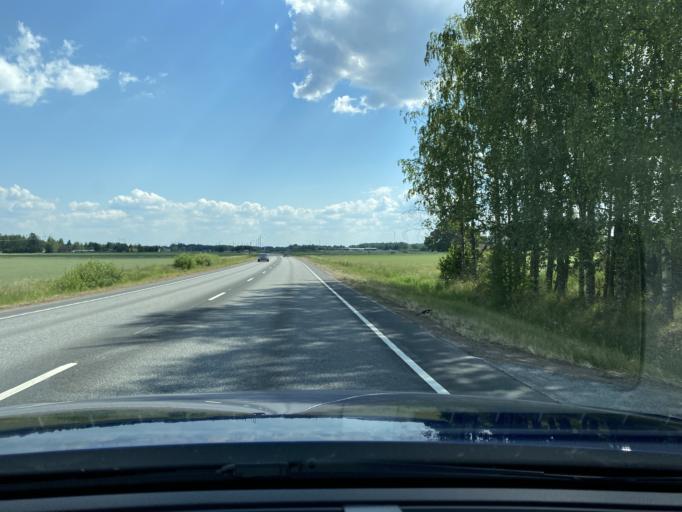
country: FI
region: Satakunta
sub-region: Rauma
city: Eura
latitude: 61.1492
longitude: 22.1006
